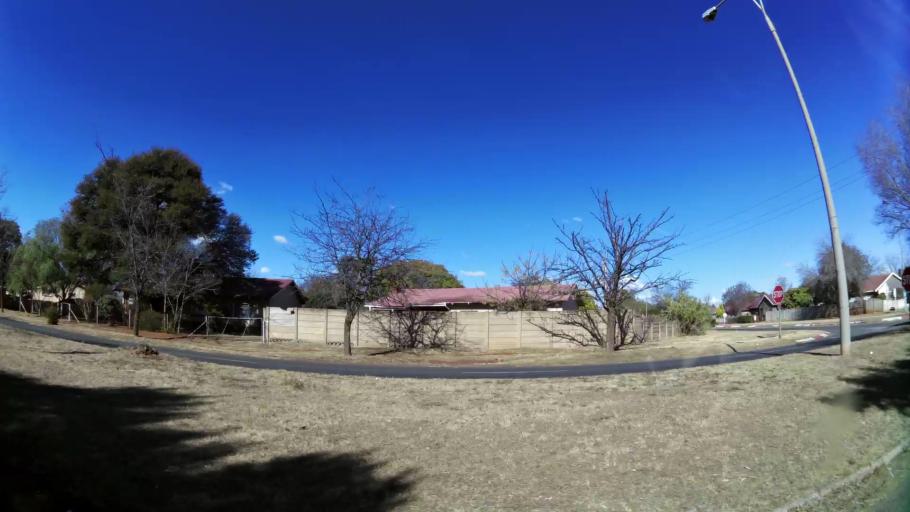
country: ZA
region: Gauteng
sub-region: West Rand District Municipality
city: Carletonville
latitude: -26.3649
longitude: 27.3790
